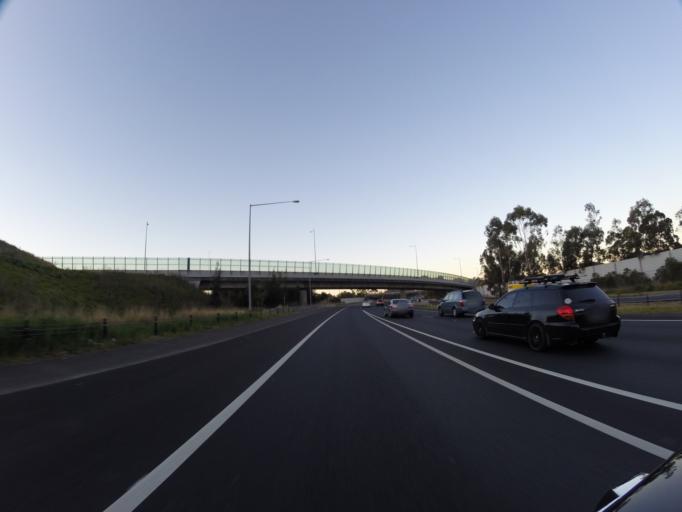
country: AU
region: New South Wales
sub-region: Campbelltown Municipality
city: Glenfield
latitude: -33.9516
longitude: 150.8798
